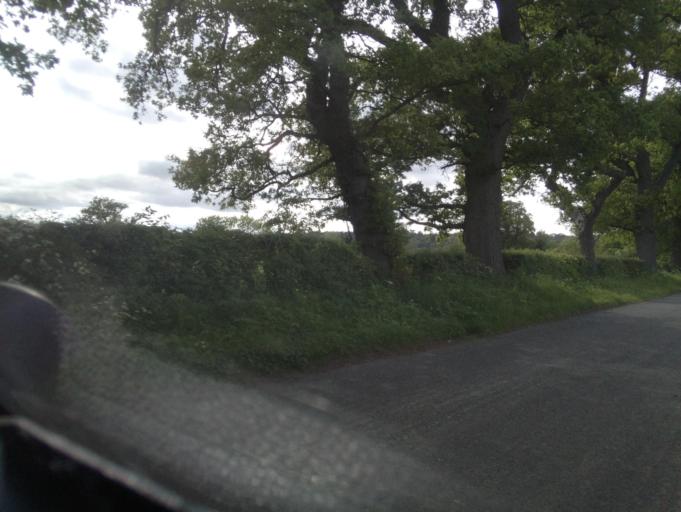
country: GB
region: England
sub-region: Gloucestershire
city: Moreton in Marsh
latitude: 51.9973
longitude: -1.7091
